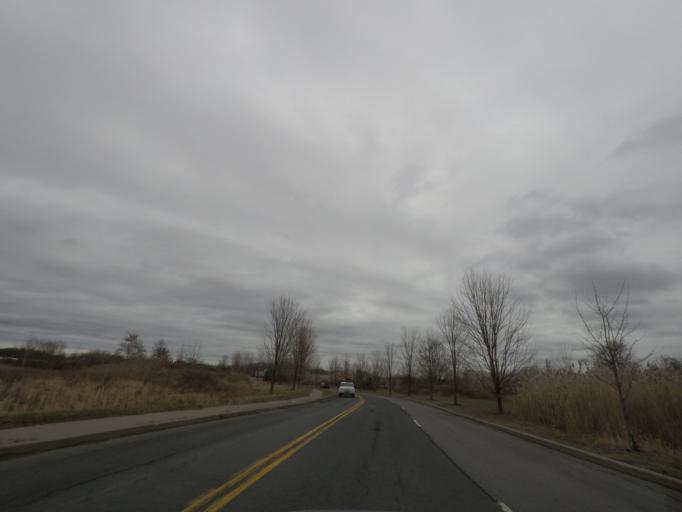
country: US
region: New York
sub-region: Albany County
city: Roessleville
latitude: 42.7577
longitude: -73.7731
